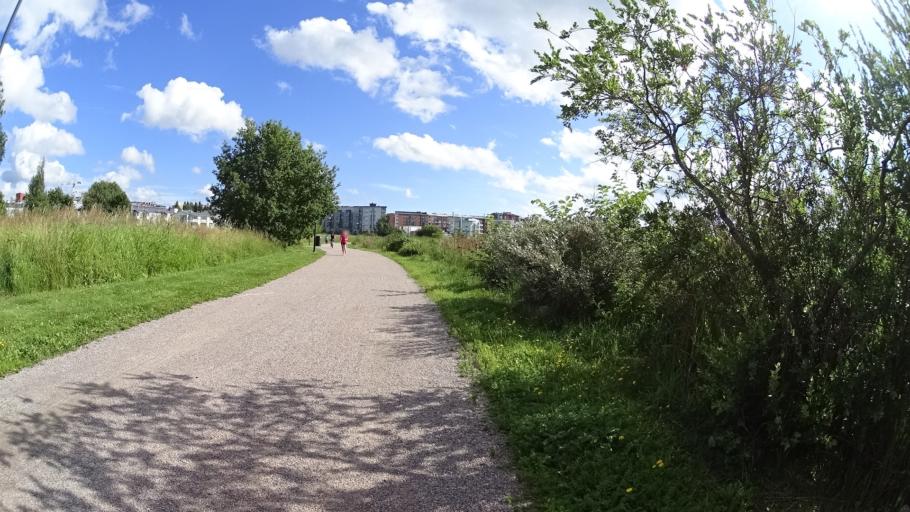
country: FI
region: Uusimaa
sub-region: Helsinki
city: Helsinki
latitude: 60.1993
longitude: 24.8917
